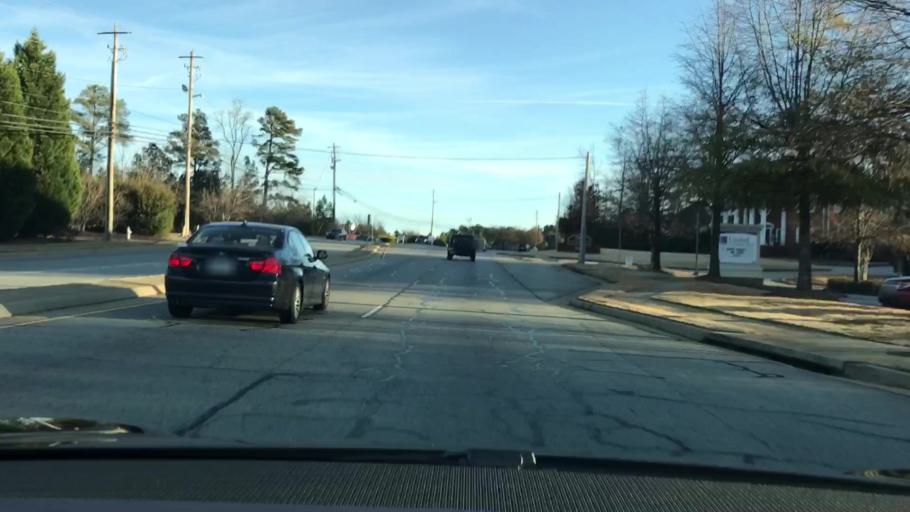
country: US
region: Georgia
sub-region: Gwinnett County
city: Buford
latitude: 34.1027
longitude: -84.0018
